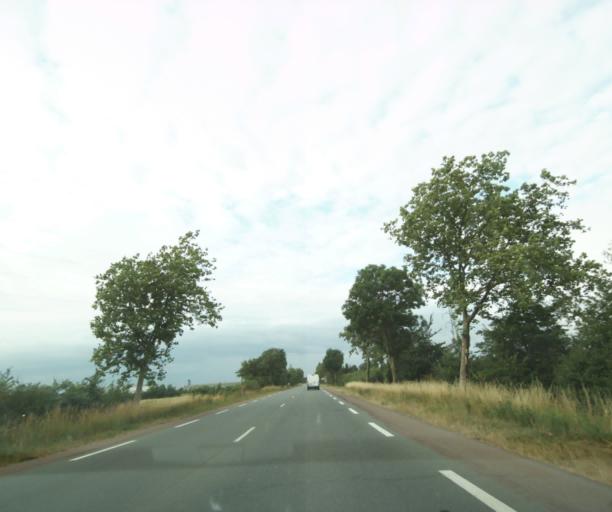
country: FR
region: Poitou-Charentes
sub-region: Departement de la Charente-Maritime
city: Marans
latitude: 46.2807
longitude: -0.9964
